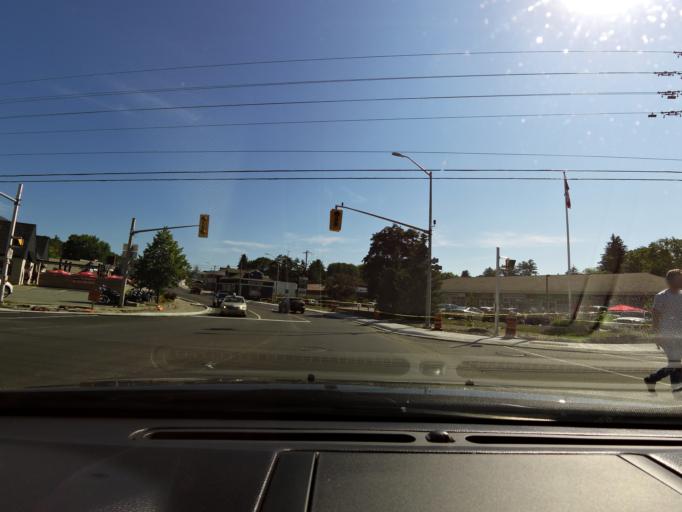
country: CA
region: Ontario
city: Huntsville
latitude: 45.3285
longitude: -79.2121
